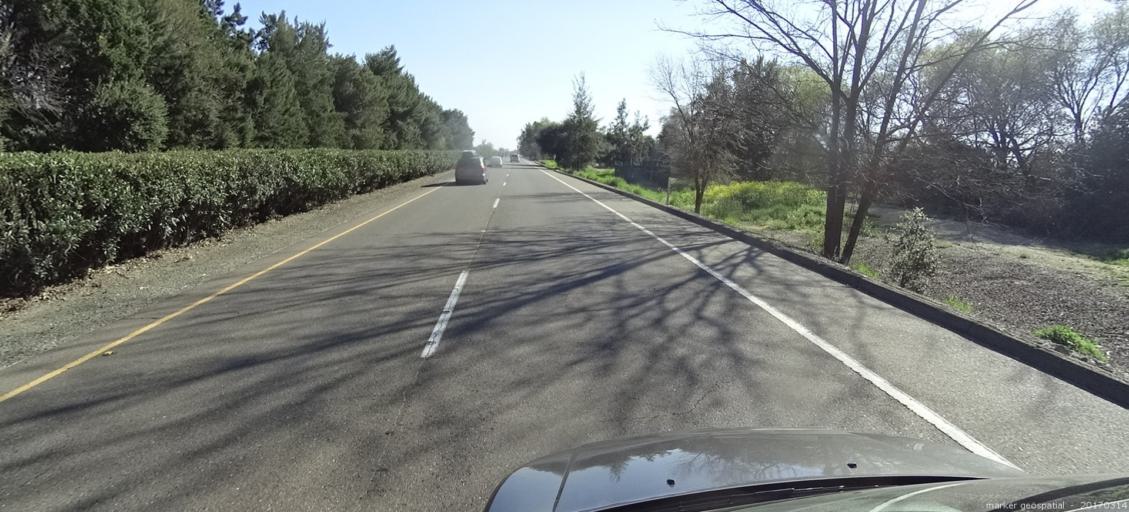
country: US
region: California
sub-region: Sacramento County
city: Parkway
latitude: 38.5025
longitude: -121.5060
